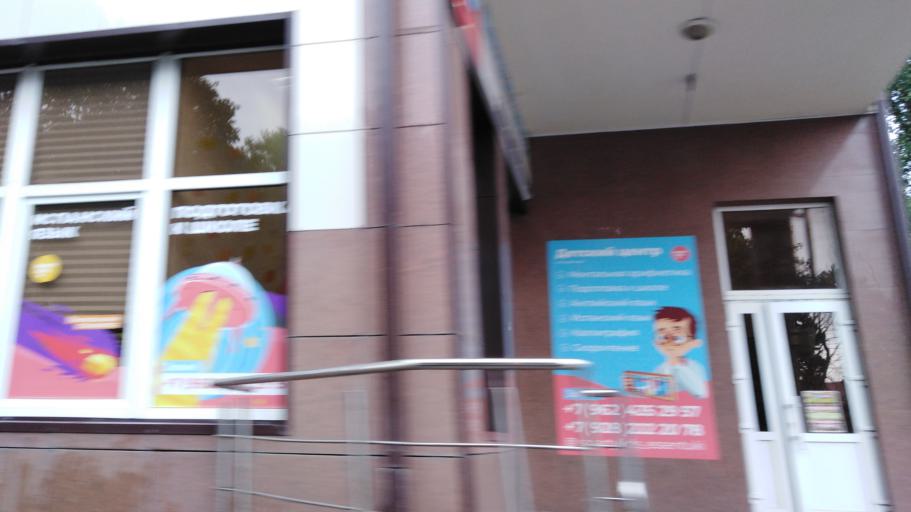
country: RU
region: Stavropol'skiy
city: Yessentukskaya
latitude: 44.0473
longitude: 42.8969
